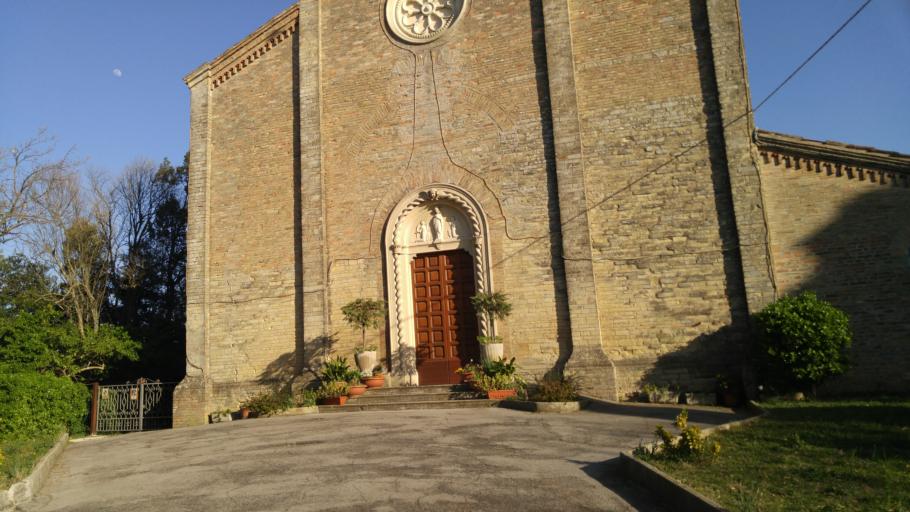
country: IT
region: The Marches
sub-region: Provincia di Pesaro e Urbino
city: Fenile
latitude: 43.8586
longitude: 12.9352
